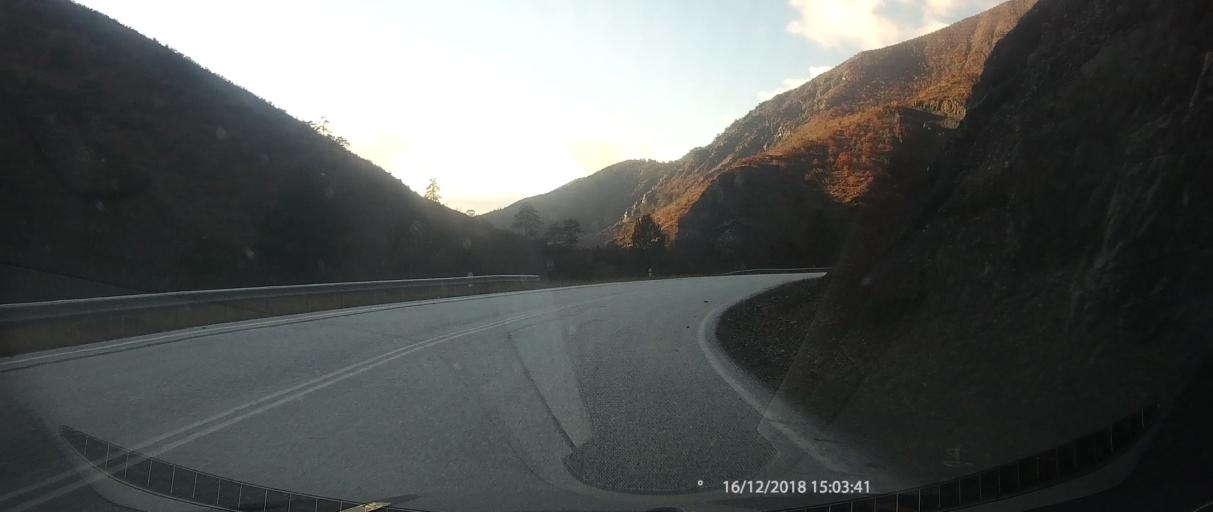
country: GR
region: West Macedonia
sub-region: Nomos Kastorias
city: Nestorio
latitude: 40.2277
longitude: 20.9789
